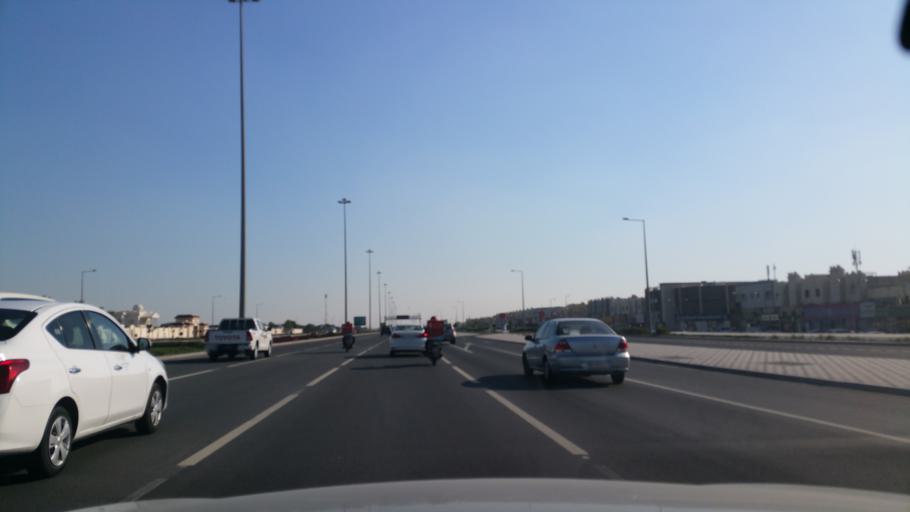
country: QA
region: Baladiyat ar Rayyan
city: Ar Rayyan
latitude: 25.2672
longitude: 51.4305
